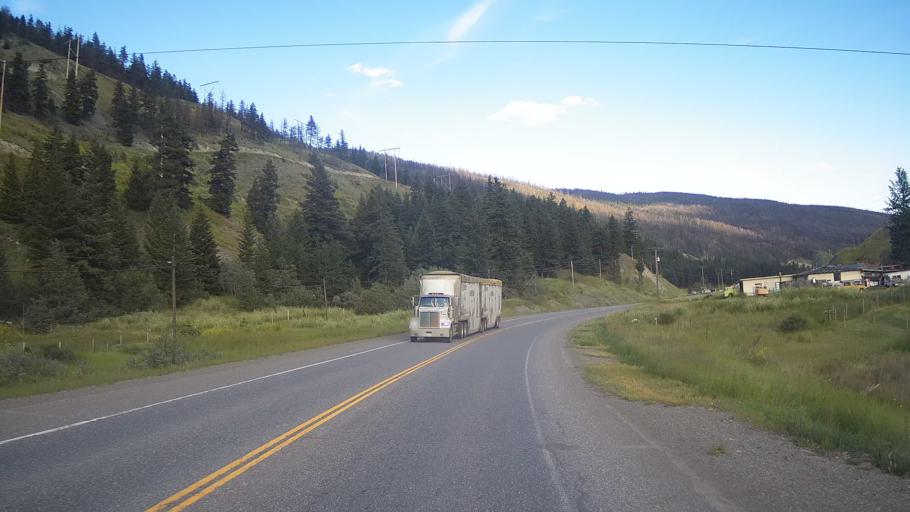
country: CA
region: British Columbia
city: Cache Creek
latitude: 51.0614
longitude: -121.5634
